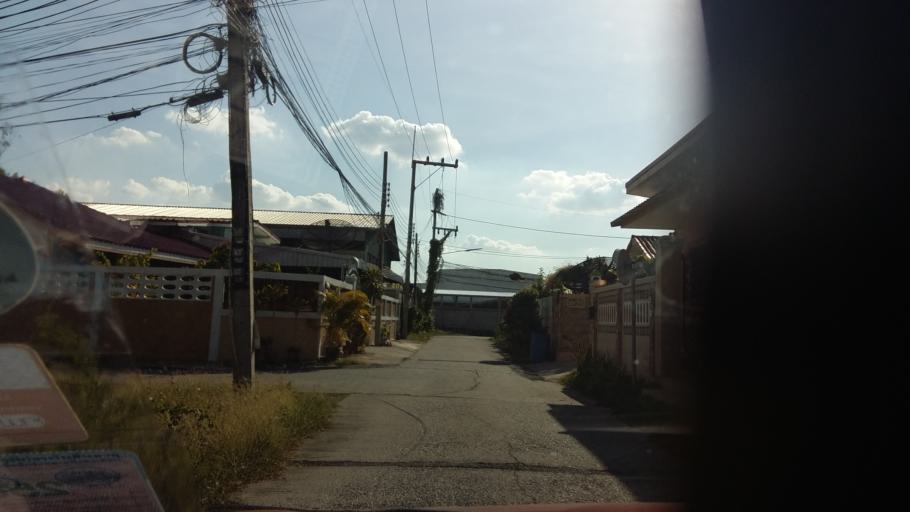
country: TH
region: Lop Buri
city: Lop Buri
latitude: 14.8298
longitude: 100.6492
